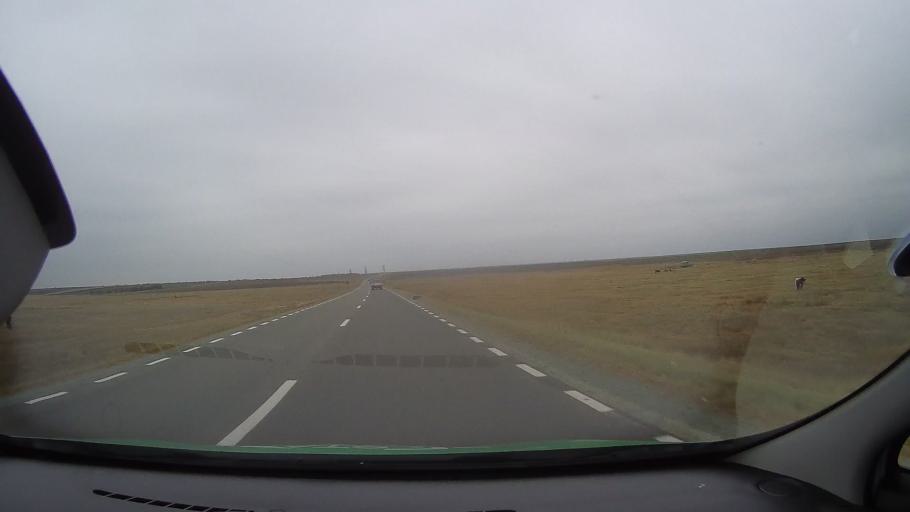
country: RO
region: Ialomita
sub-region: Comuna Scanteia
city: Iazu
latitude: 44.7251
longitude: 27.4230
